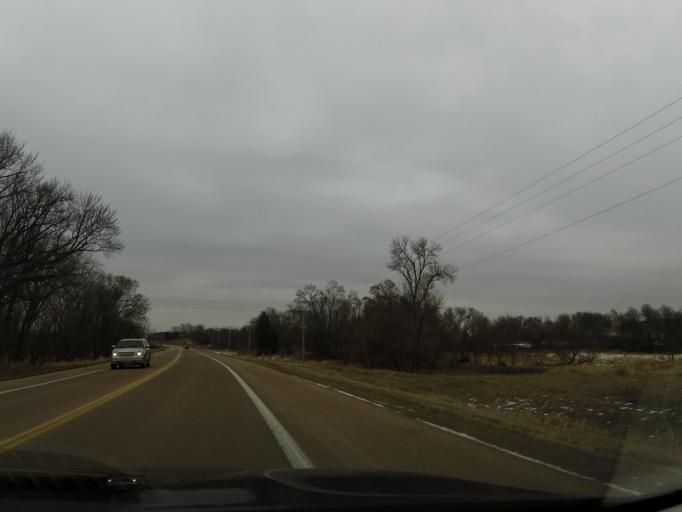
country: US
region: Minnesota
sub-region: Hennepin County
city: Minnetrista
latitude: 44.9736
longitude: -93.7729
